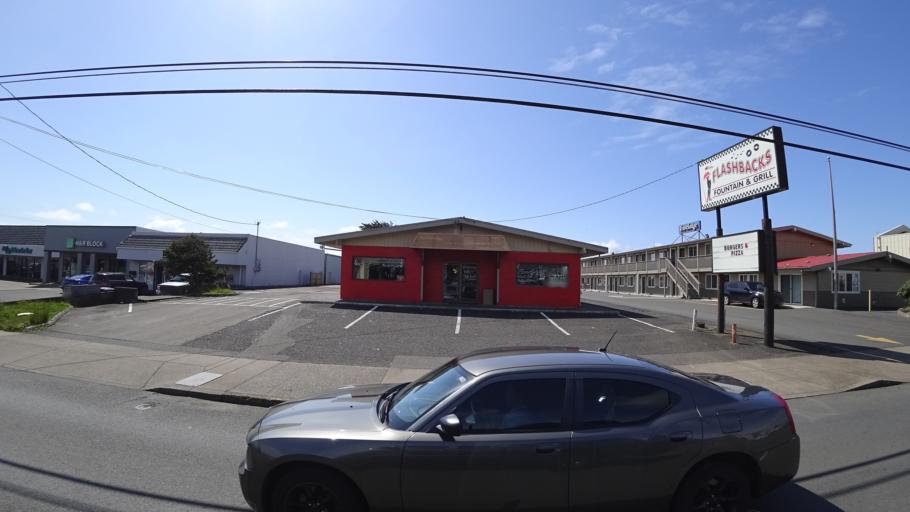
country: US
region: Oregon
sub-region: Lincoln County
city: Newport
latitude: 44.6465
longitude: -124.0531
